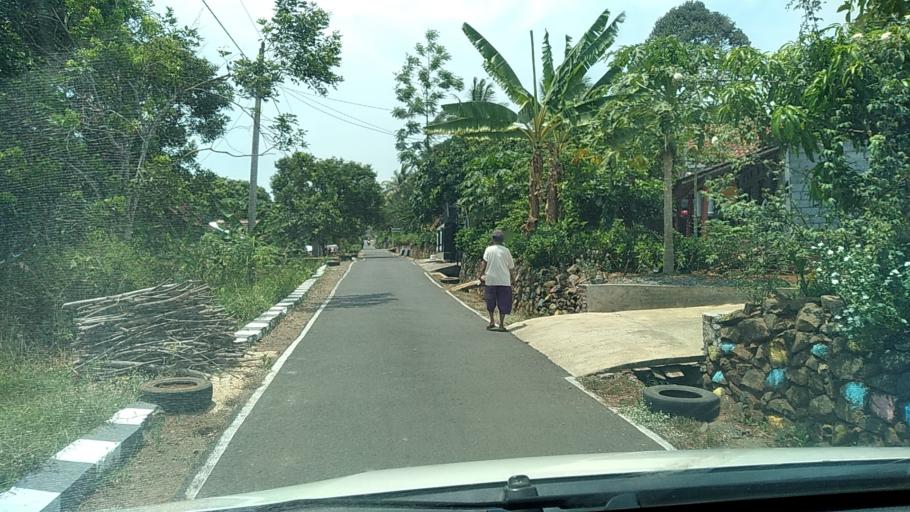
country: ID
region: Central Java
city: Ungaran
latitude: -7.0979
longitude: 110.3442
